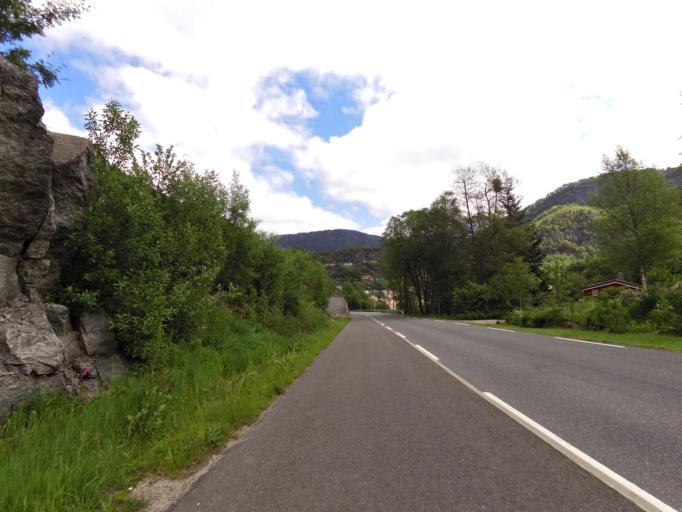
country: NO
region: Vest-Agder
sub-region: Flekkefjord
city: Flekkefjord
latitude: 58.2685
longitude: 6.8086
